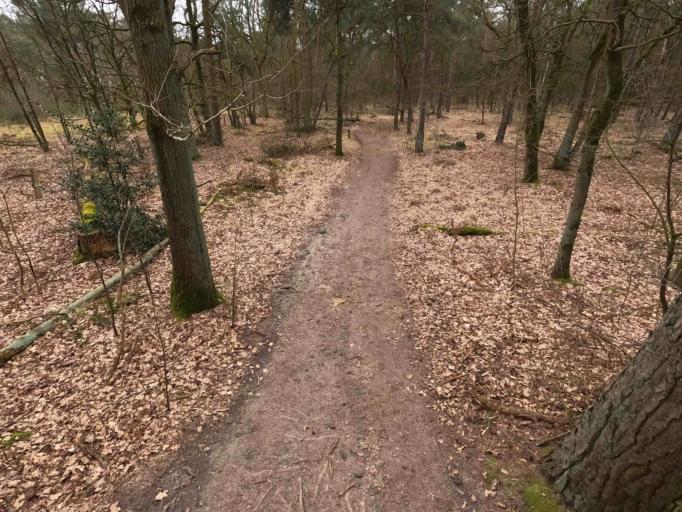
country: BE
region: Flanders
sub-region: Provincie Antwerpen
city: Stabroek
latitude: 51.4157
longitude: 4.3930
